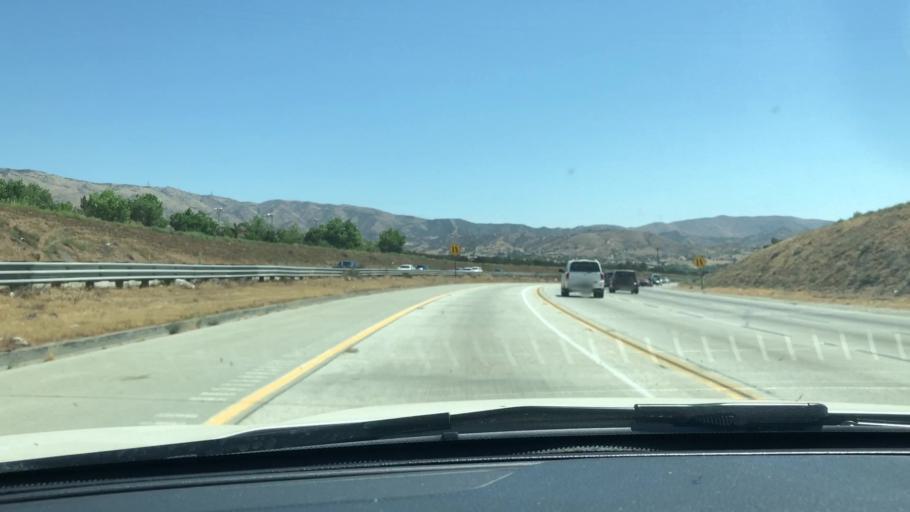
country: US
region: California
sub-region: Los Angeles County
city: Acton
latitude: 34.5024
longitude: -118.2513
